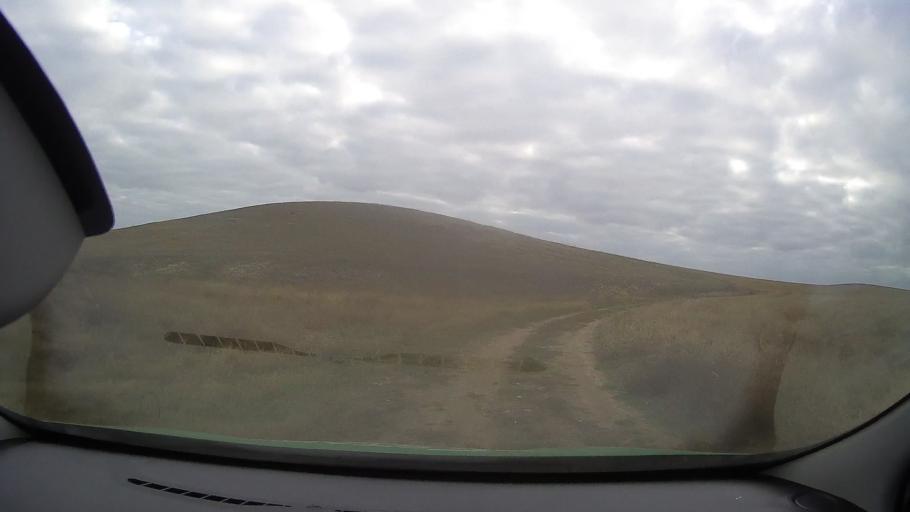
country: RO
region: Tulcea
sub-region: Comuna Jurilovca
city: Jurilovca
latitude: 44.7670
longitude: 28.9217
